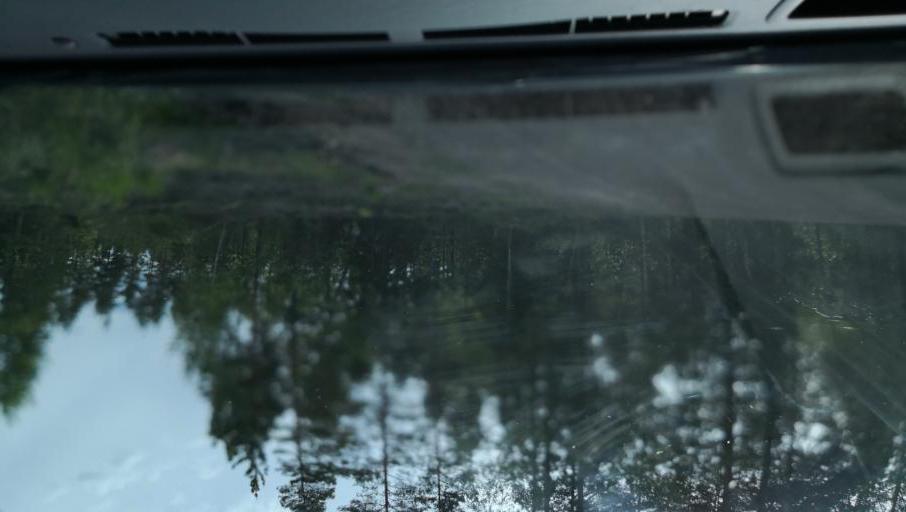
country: SE
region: Vaestmanland
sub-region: Arboga Kommun
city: Tyringe
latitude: 59.3458
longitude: 15.9288
